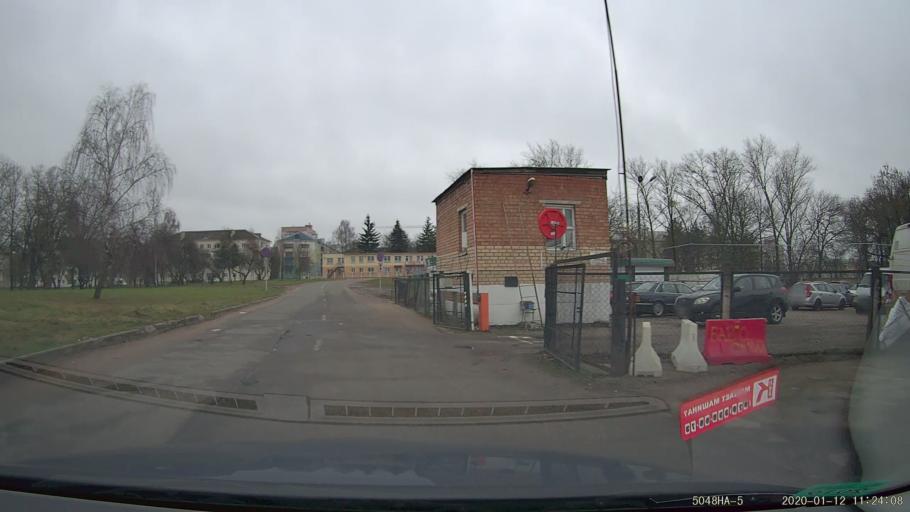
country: BY
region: Minsk
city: Minsk
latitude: 53.8976
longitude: 27.5132
